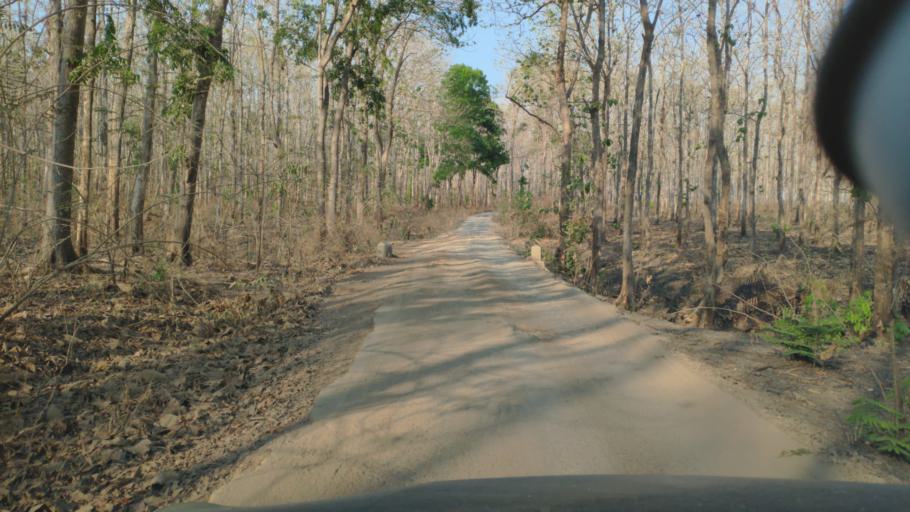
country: ID
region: Central Java
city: Sendangrejo
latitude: -6.9182
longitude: 111.5516
